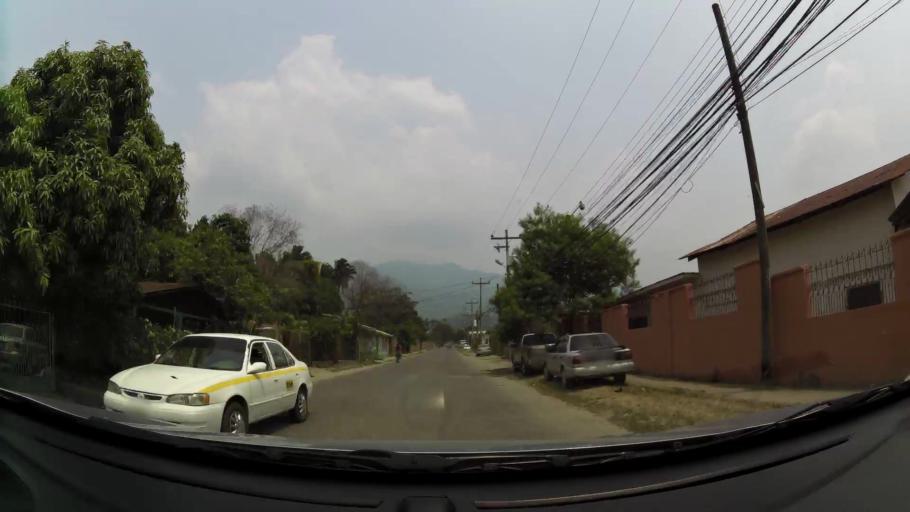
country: HN
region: Yoro
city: El Progreso
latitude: 15.3958
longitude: -87.7972
